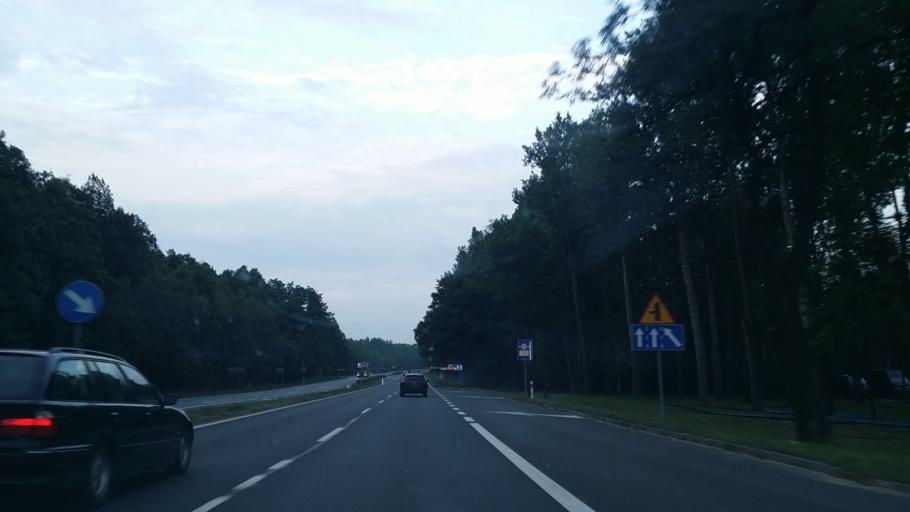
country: PL
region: Lower Silesian Voivodeship
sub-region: Powiat lubinski
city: Lubin
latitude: 51.4323
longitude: 16.1649
